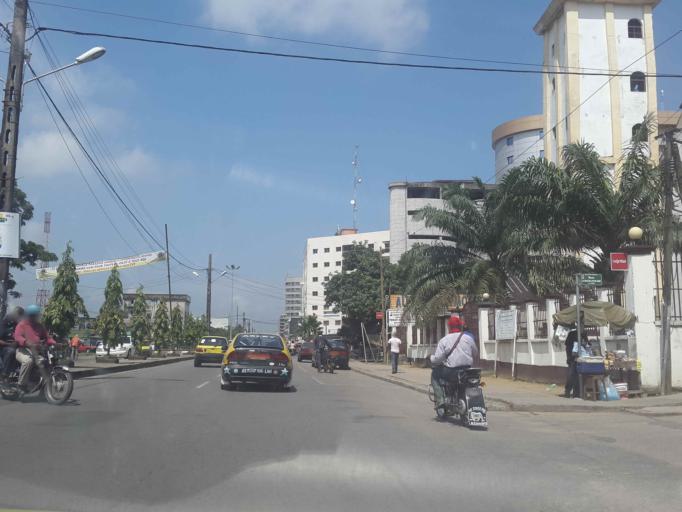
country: CM
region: Littoral
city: Douala
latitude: 4.0514
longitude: 9.7030
